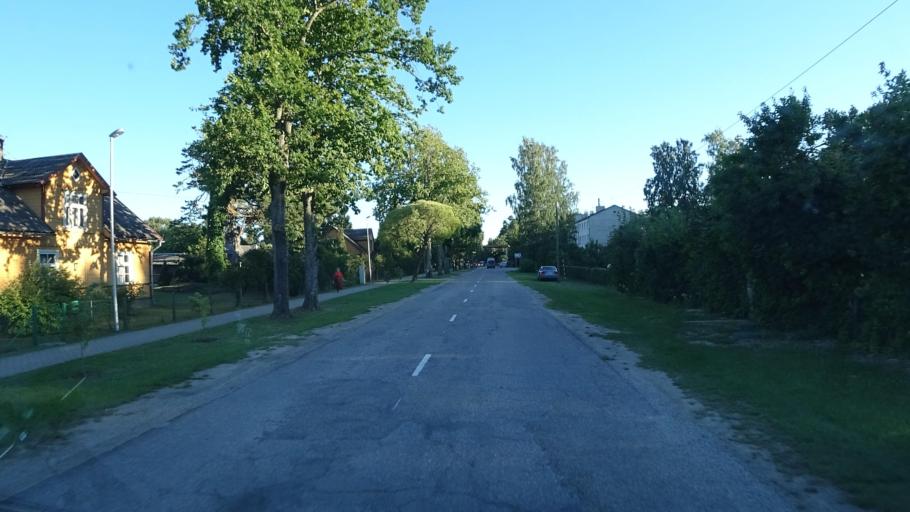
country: LV
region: Dundaga
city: Dundaga
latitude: 57.7397
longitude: 22.5829
